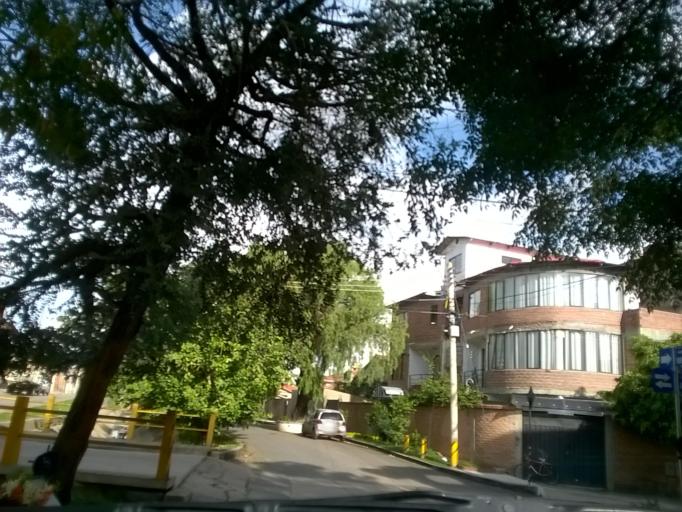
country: BO
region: Cochabamba
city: Cochabamba
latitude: -17.3655
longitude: -66.1811
